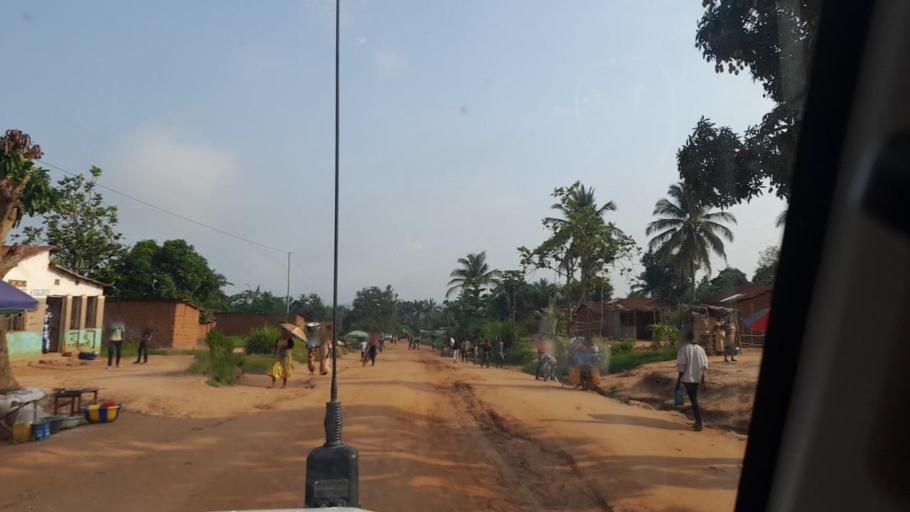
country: CD
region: Kasai-Occidental
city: Kananga
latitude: -5.8957
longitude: 22.3758
